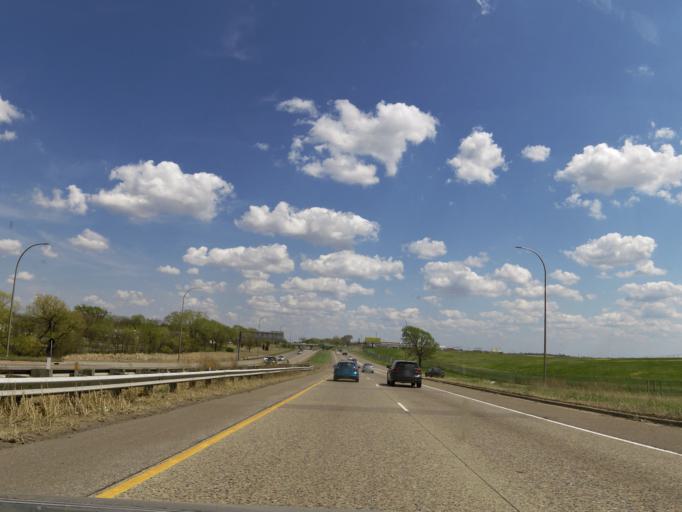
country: US
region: Minnesota
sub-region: Hennepin County
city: Richfield
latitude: 44.8973
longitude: -93.2303
